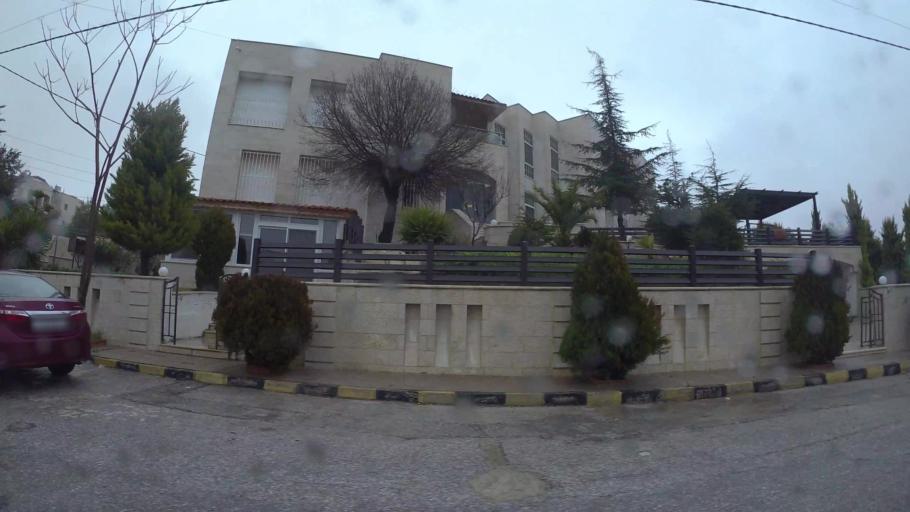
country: JO
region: Amman
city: Wadi as Sir
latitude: 32.0047
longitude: 35.7950
